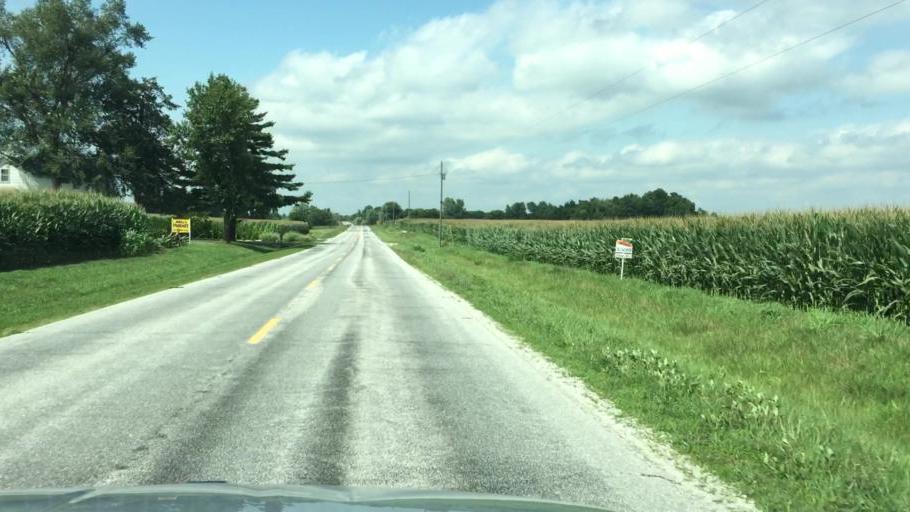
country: US
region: Illinois
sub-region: Hancock County
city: Nauvoo
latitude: 40.5171
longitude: -91.3079
